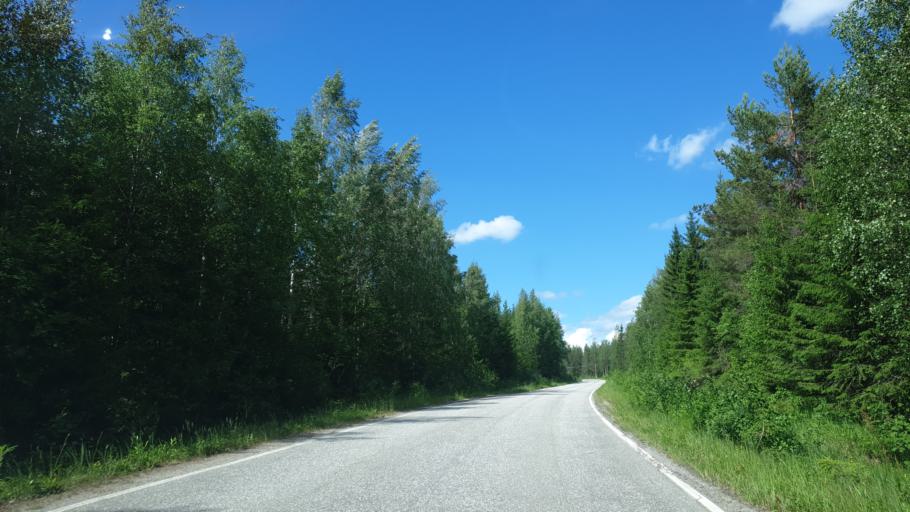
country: FI
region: Northern Savo
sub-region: Koillis-Savo
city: Kaavi
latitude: 63.0381
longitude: 28.5994
